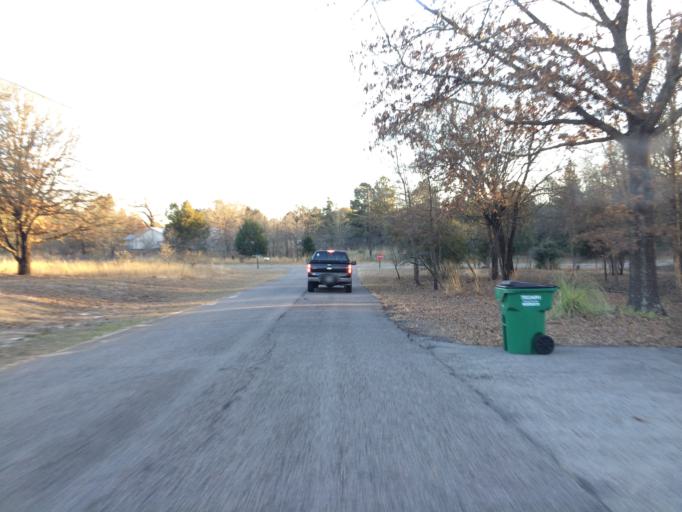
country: US
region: Texas
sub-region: Wood County
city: Hawkins
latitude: 32.7212
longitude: -95.1742
